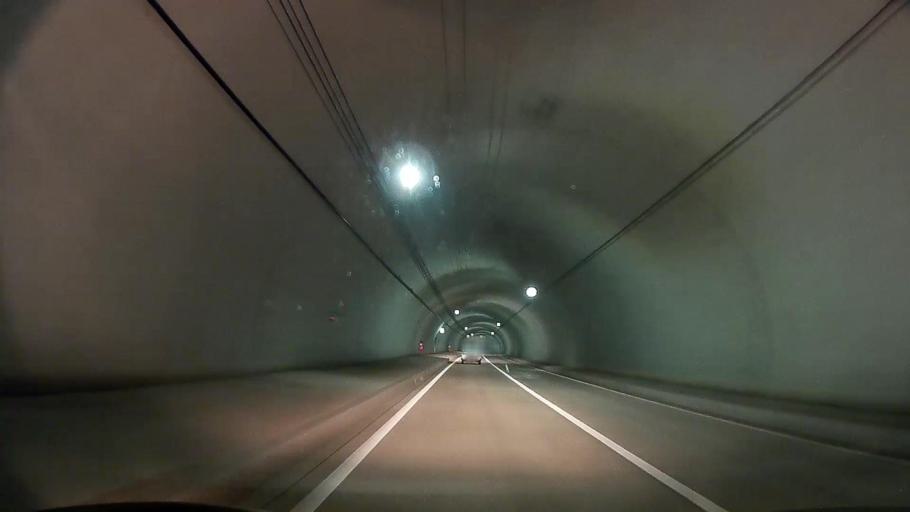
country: JP
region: Gunma
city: Nakanojomachi
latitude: 36.5313
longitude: 138.7151
